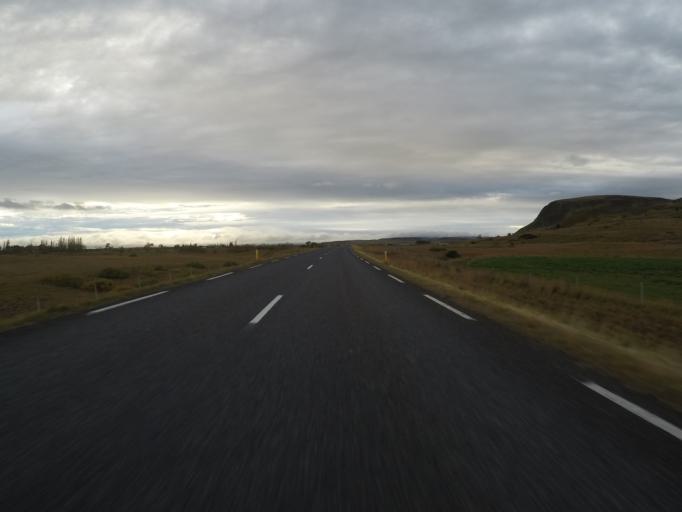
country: IS
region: South
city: Vestmannaeyjar
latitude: 64.0411
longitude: -20.2061
